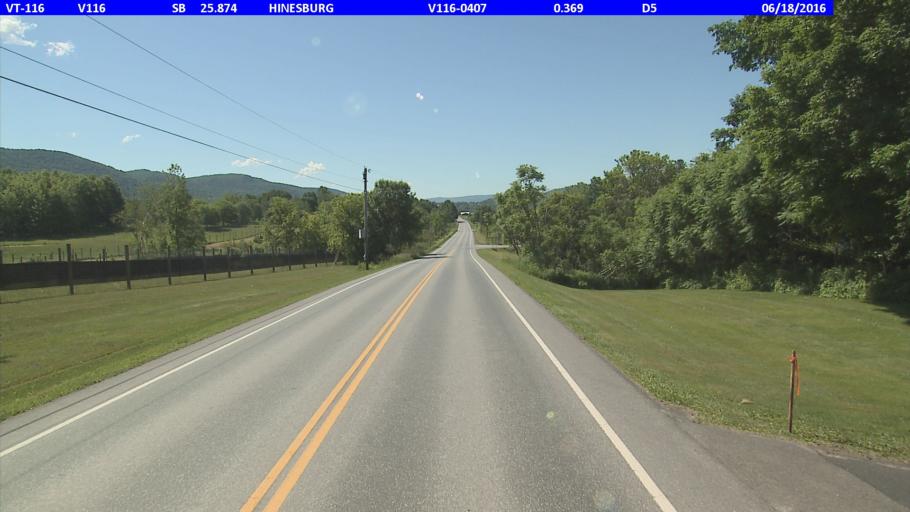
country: US
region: Vermont
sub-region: Chittenden County
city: Hinesburg
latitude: 44.2854
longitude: -73.0692
